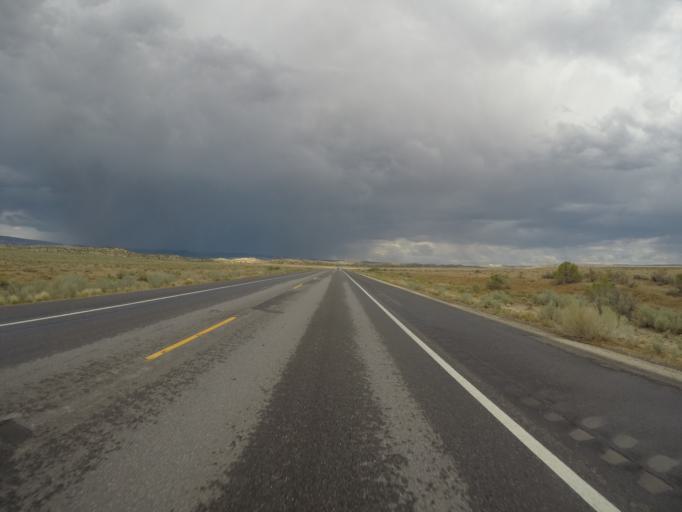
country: US
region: Colorado
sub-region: Rio Blanco County
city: Rangely
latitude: 40.2830
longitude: -109.0992
